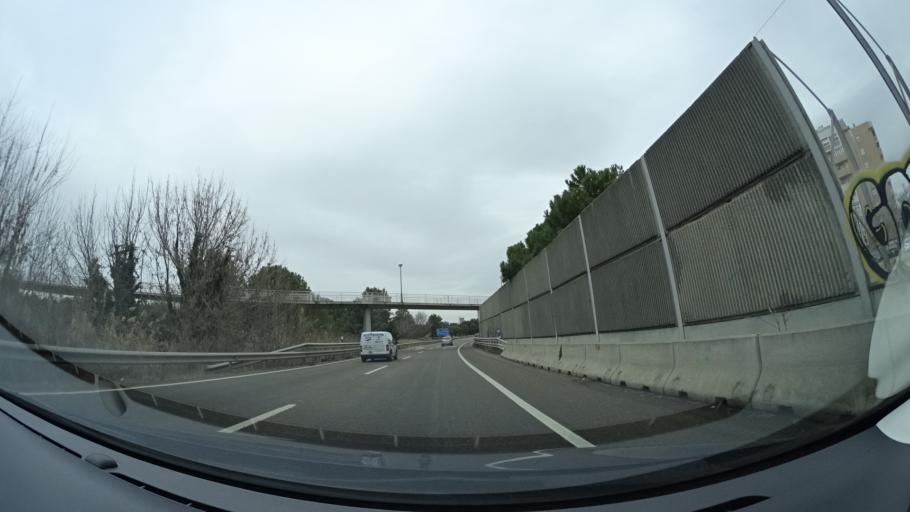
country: ES
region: Aragon
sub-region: Provincia de Zaragoza
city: Zaragoza
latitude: 41.6754
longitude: -0.8798
